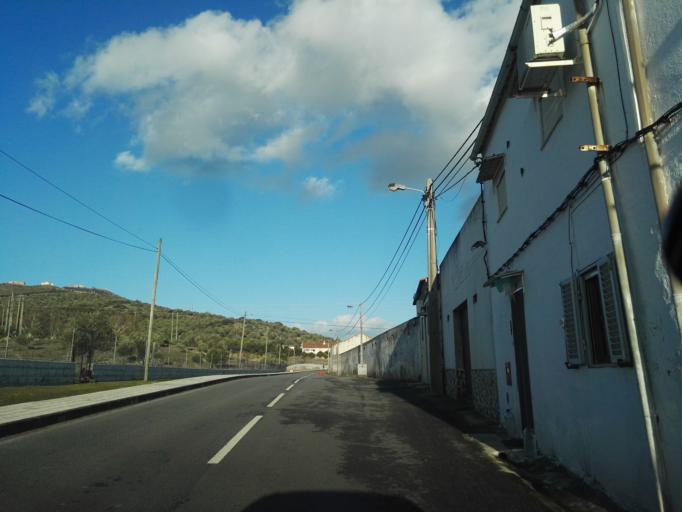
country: PT
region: Portalegre
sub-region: Elvas
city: Elvas
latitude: 38.8849
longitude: -7.1695
